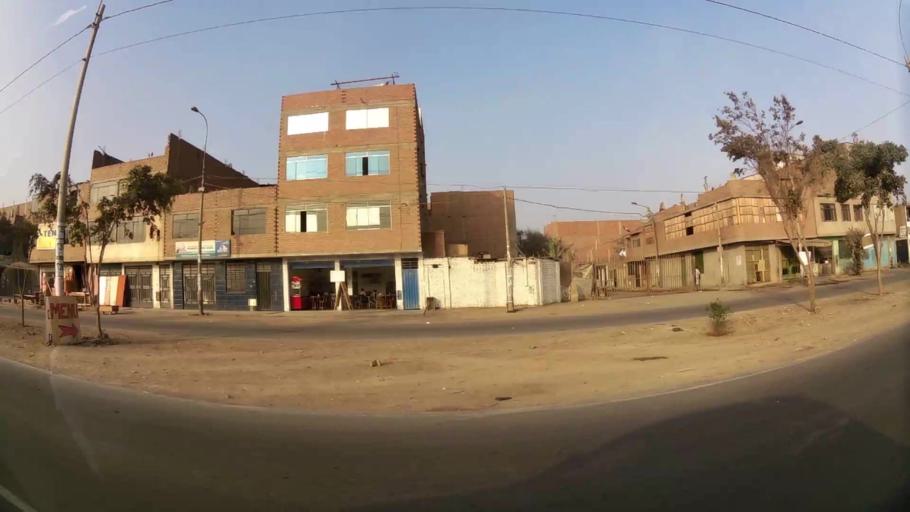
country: PE
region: Lima
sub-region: Lima
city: Independencia
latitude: -11.9592
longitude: -77.0842
